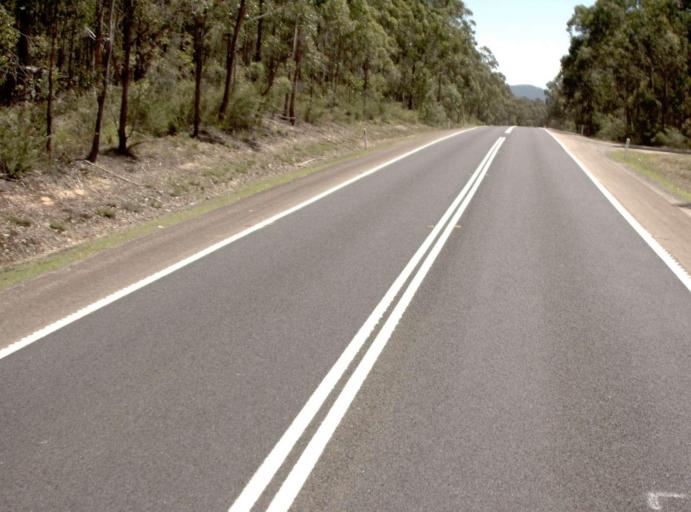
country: AU
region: New South Wales
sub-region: Bombala
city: Bombala
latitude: -37.5657
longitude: 149.1017
